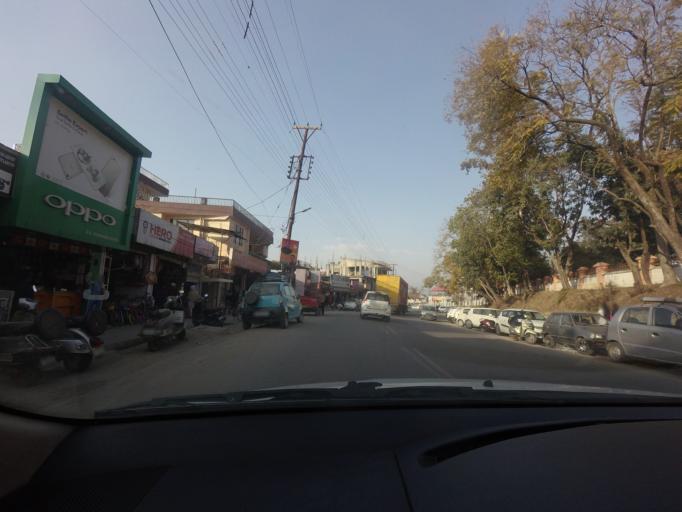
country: IN
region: Himachal Pradesh
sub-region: Mandi
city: Sundarnagar
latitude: 31.5281
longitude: 76.8885
